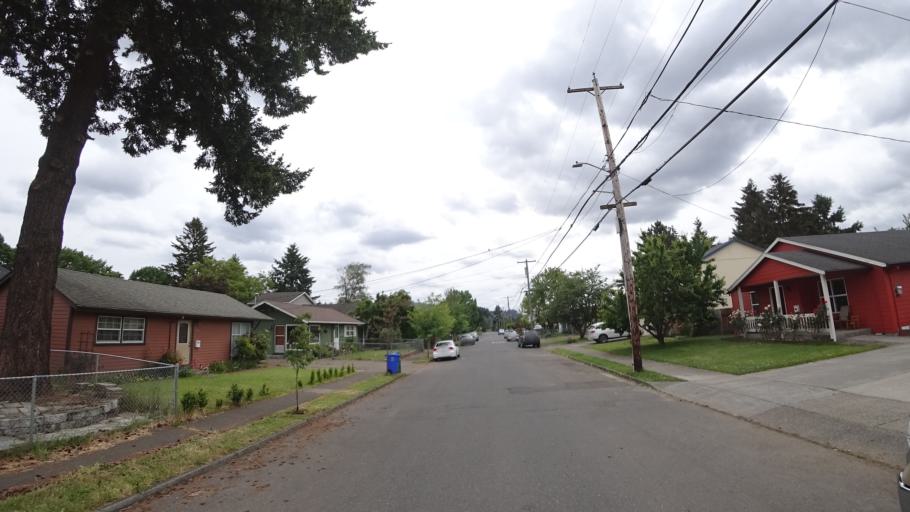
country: US
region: Oregon
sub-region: Multnomah County
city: Lents
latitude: 45.4861
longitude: -122.5622
